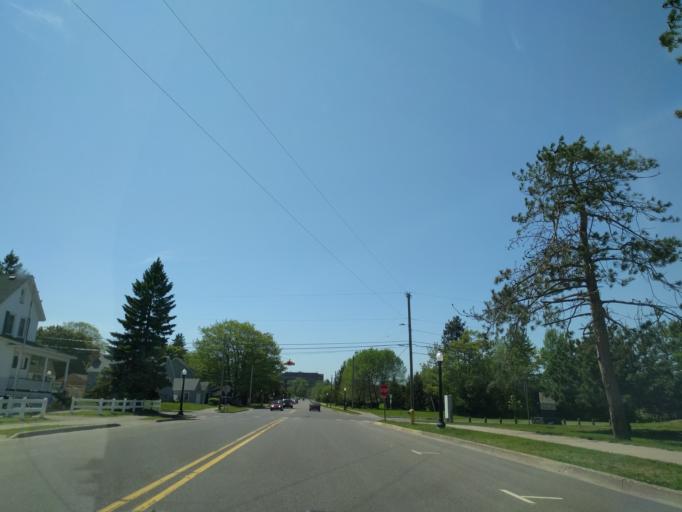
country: US
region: Michigan
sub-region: Marquette County
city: Marquette
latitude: 46.5565
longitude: -87.3886
